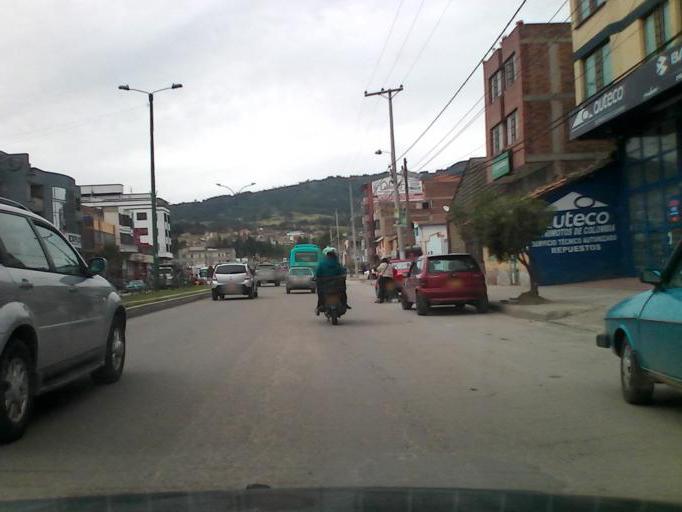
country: CO
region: Boyaca
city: Duitama
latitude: 5.8203
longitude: -73.0359
